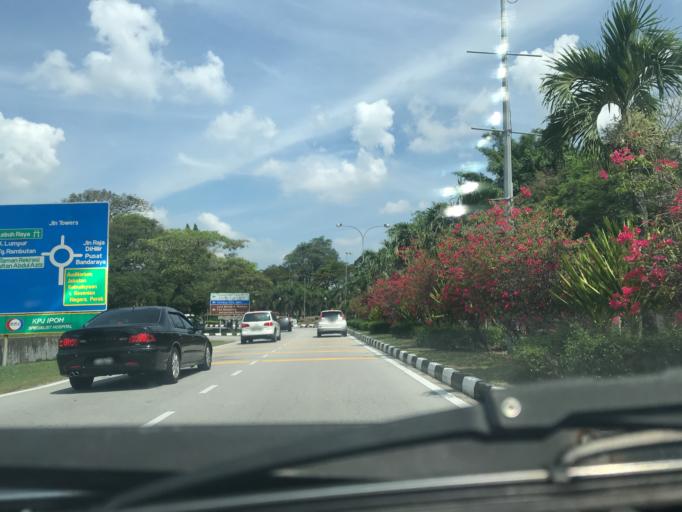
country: MY
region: Perak
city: Ipoh
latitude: 4.5987
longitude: 101.1052
